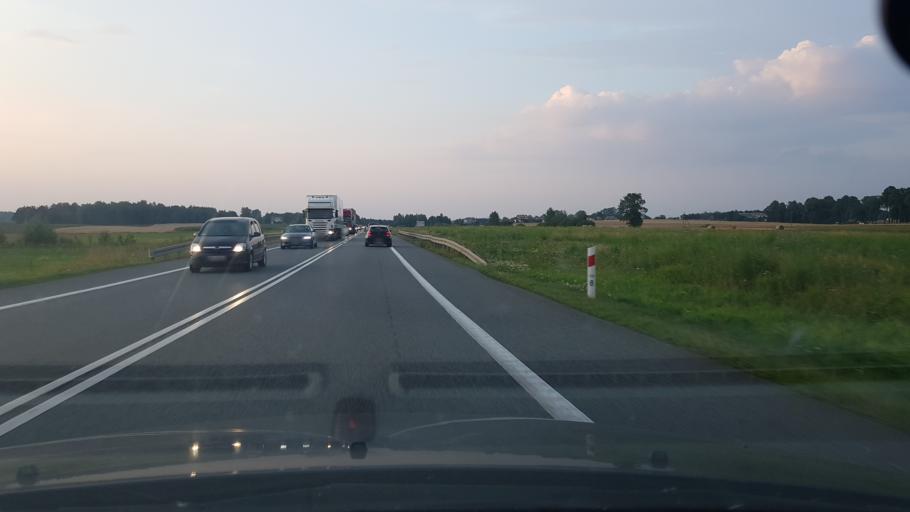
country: PL
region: Masovian Voivodeship
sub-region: Powiat mlawski
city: Wieczfnia Koscielna
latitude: 53.1798
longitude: 20.4293
